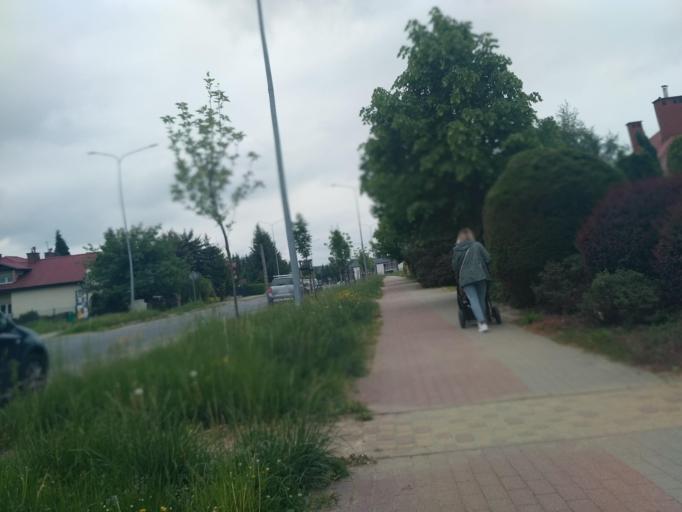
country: PL
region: Subcarpathian Voivodeship
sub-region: Krosno
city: Krosno
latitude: 49.6791
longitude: 21.7599
